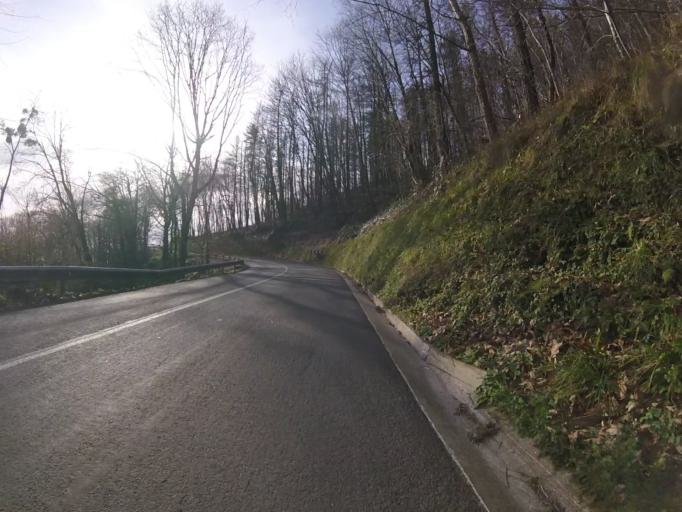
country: ES
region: Basque Country
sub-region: Provincia de Guipuzcoa
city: Asteasu
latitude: 43.2020
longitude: -2.1159
